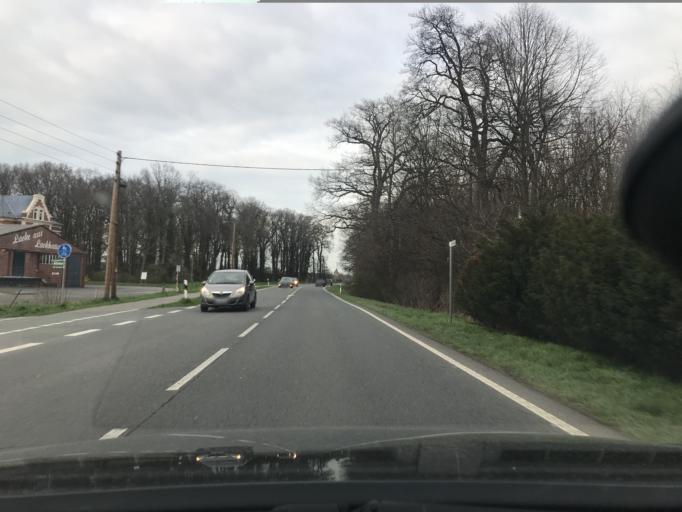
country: DE
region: North Rhine-Westphalia
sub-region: Regierungsbezirk Dusseldorf
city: Wesel
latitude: 51.6828
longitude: 6.6524
